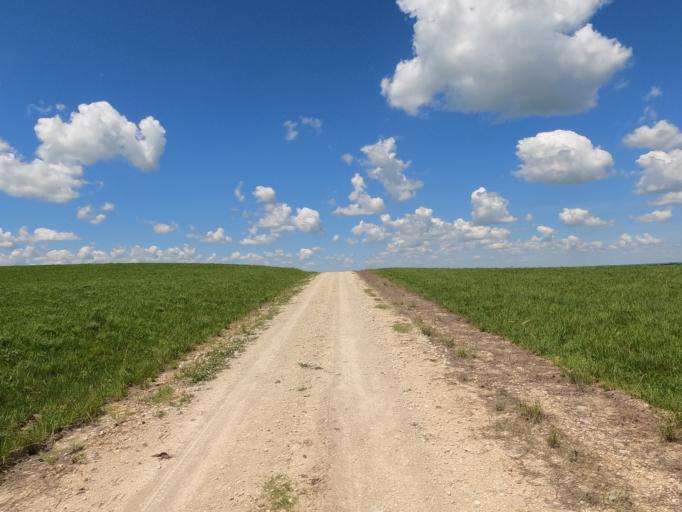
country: US
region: Kansas
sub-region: Marion County
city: Marion
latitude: 38.2419
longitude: -96.7909
